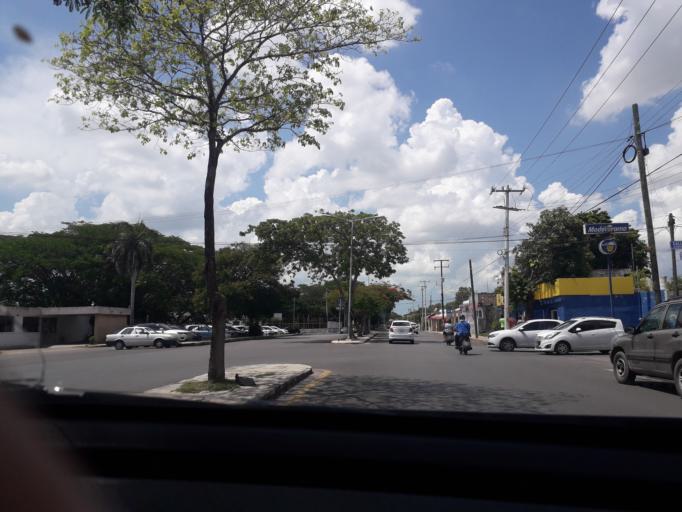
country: MX
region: Yucatan
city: Merida
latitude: 20.9728
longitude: -89.6558
